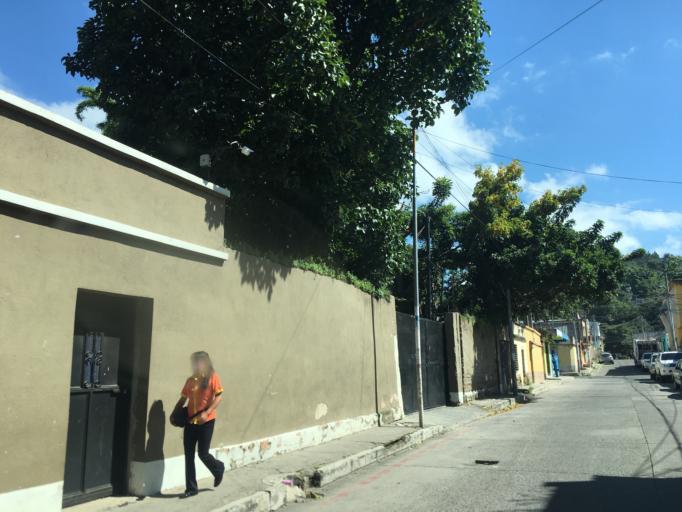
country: GT
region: Guatemala
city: Villa Canales
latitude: 14.4837
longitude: -90.5324
